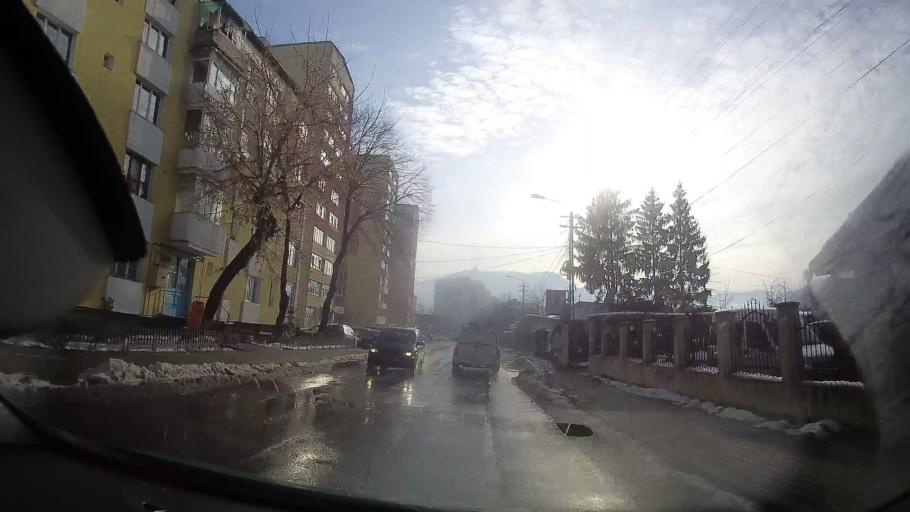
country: RO
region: Neamt
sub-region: Municipiul Piatra-Neamt
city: Valeni
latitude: 46.9424
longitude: 26.3822
